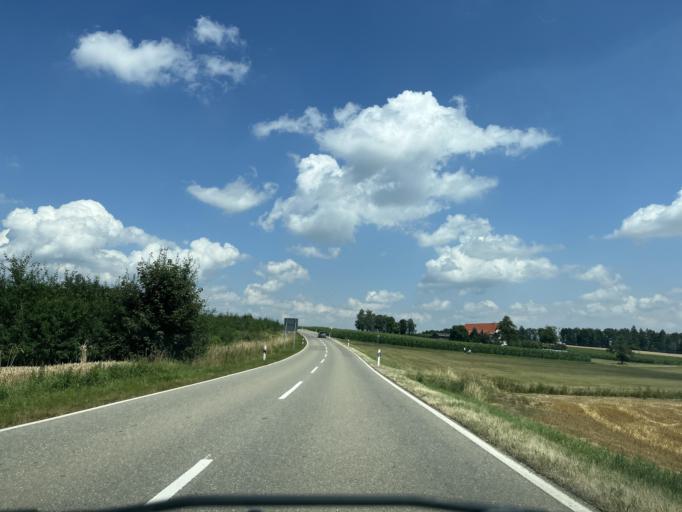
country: DE
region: Baden-Wuerttemberg
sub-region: Tuebingen Region
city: Wald
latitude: 47.9676
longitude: 9.1991
